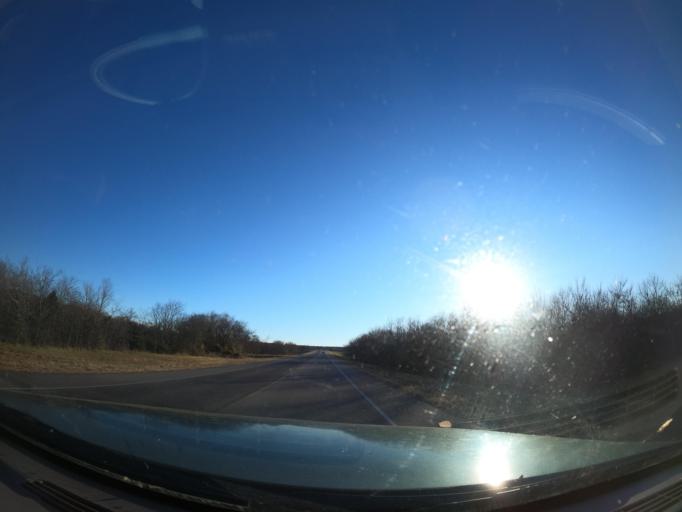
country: US
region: Oklahoma
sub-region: Pittsburg County
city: Hartshorne
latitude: 34.8516
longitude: -95.5357
